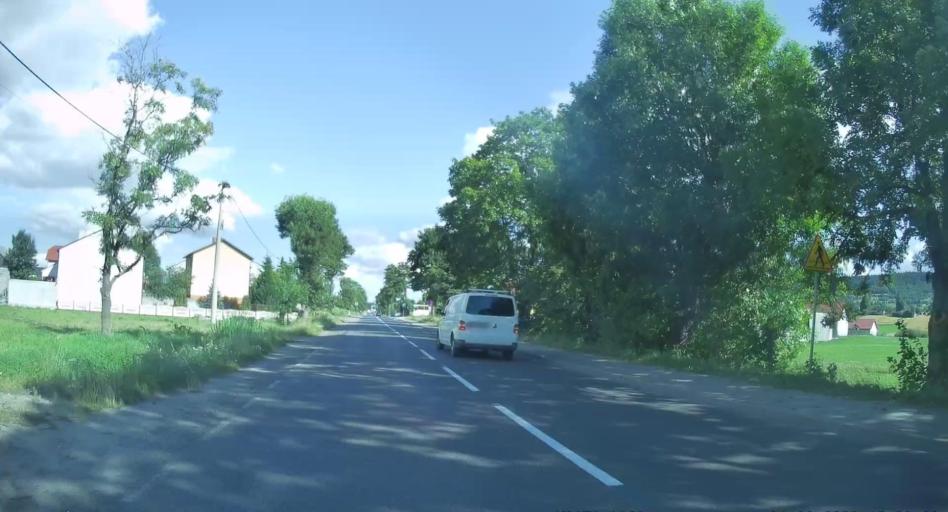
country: PL
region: Swietokrzyskie
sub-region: Powiat kielecki
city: Bodzentyn
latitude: 50.9482
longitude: 20.9330
